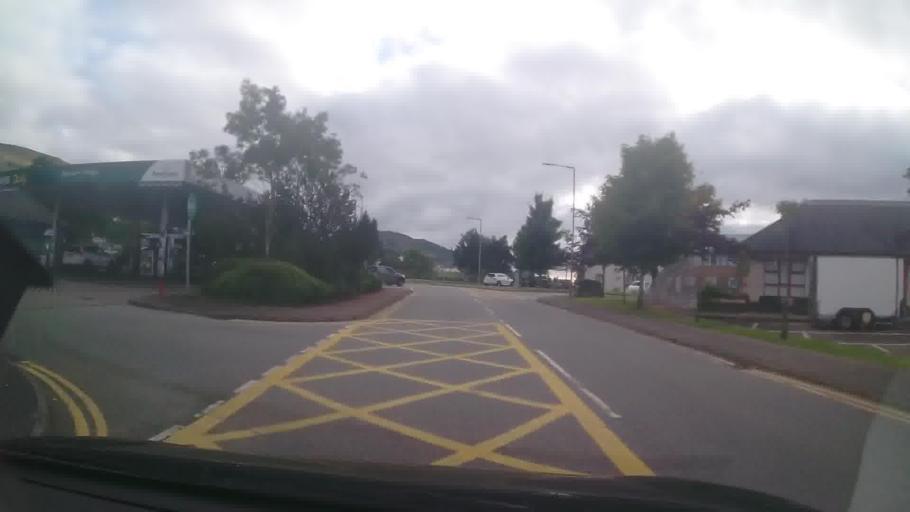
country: GB
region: Scotland
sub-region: Highland
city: Fort William
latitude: 56.8230
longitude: -5.1067
